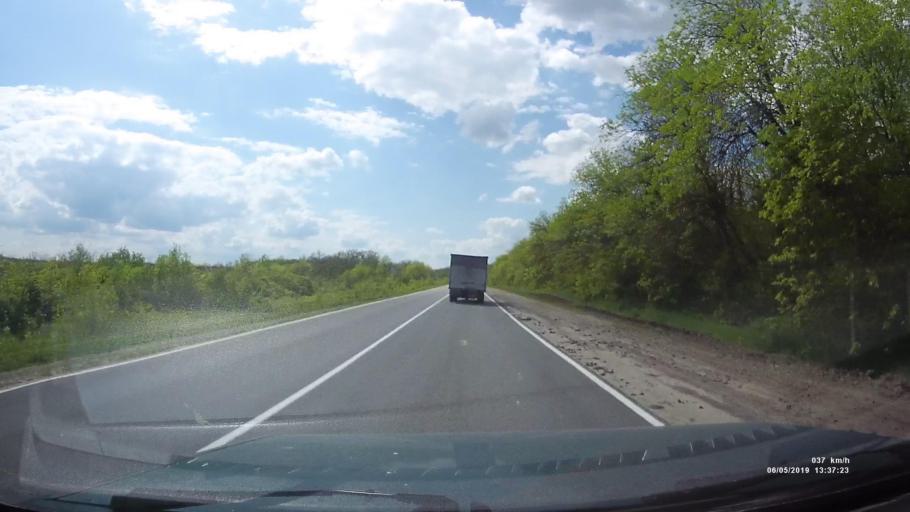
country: RU
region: Rostov
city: Ust'-Donetskiy
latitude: 47.6895
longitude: 40.7199
